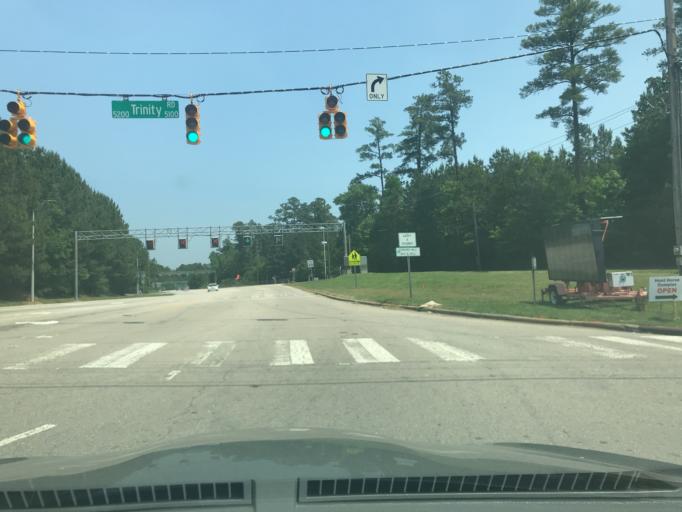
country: US
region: North Carolina
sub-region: Wake County
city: Cary
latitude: 35.7997
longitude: -78.7272
